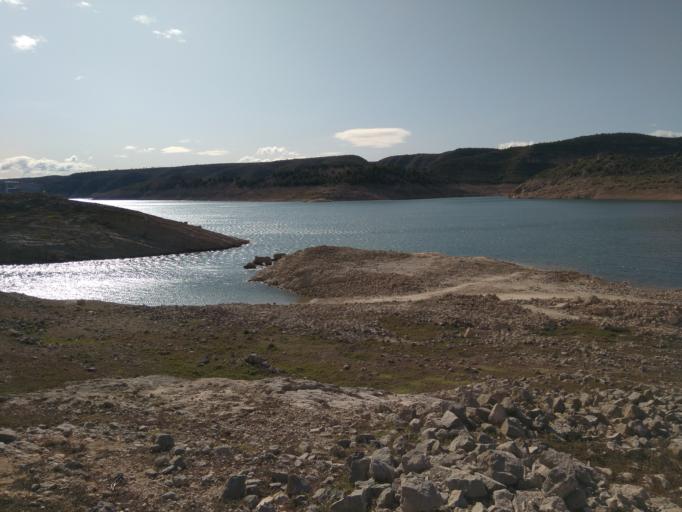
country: ES
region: Valencia
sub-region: Provincia de Valencia
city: Sumacarcer
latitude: 39.1559
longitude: -0.6593
